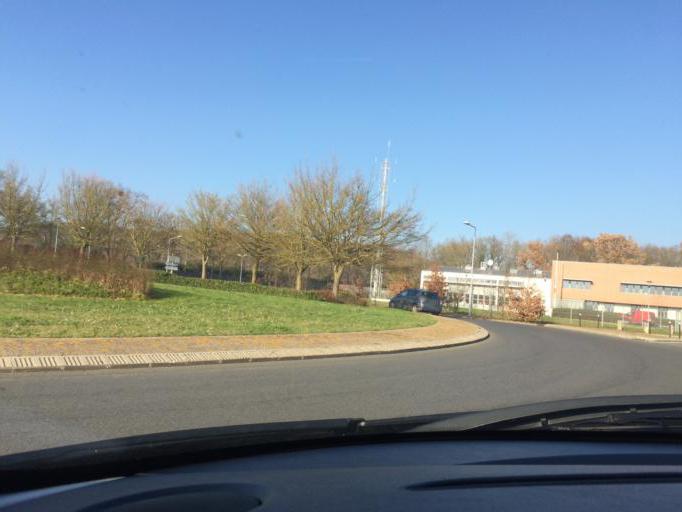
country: FR
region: Ile-de-France
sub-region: Departement de l'Essonne
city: Bouray-sur-Juine
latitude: 48.5262
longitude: 2.2885
